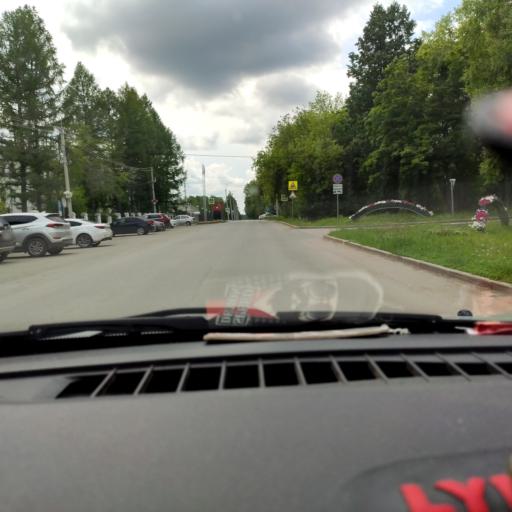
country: RU
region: Perm
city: Zvezdnyy
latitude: 57.7342
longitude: 56.3133
